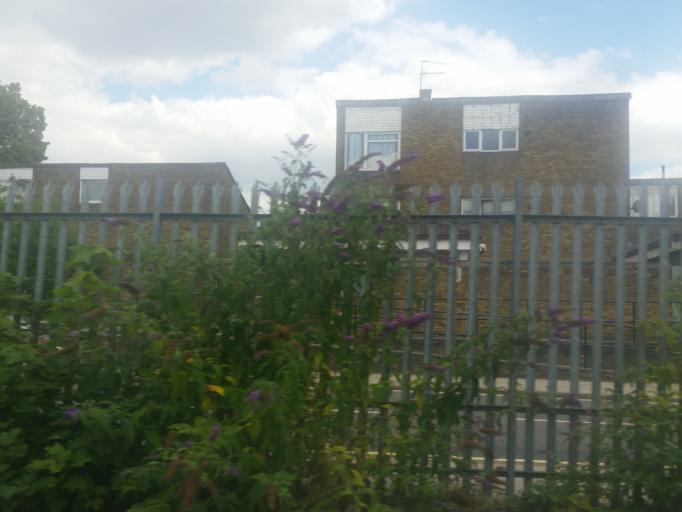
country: GB
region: England
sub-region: Greater London
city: Brixton
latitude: 51.4547
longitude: -0.1028
